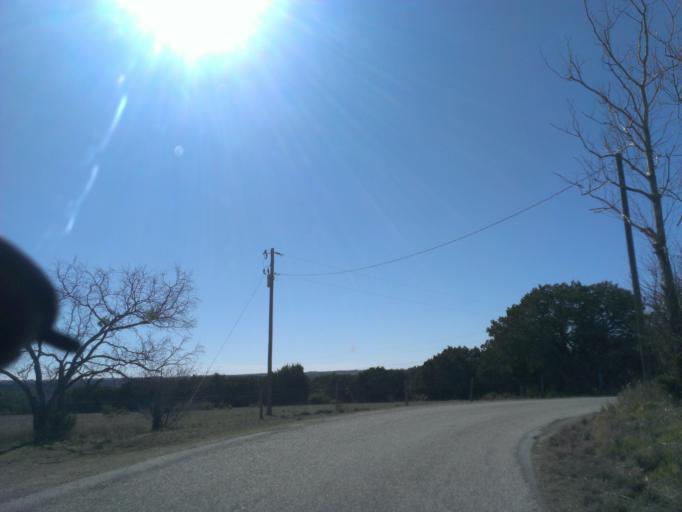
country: US
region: Texas
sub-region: Burnet County
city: Bertram
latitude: 30.9136
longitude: -98.0723
